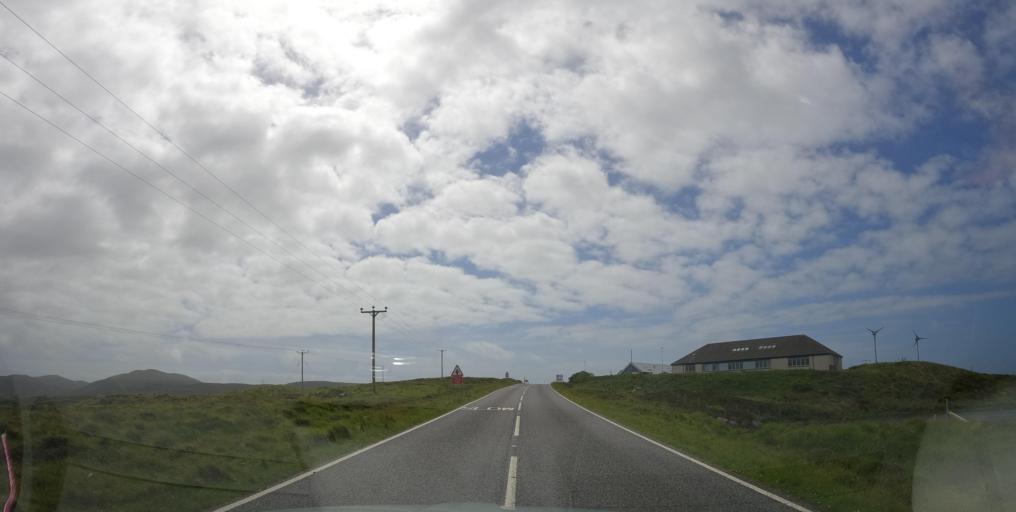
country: GB
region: Scotland
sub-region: Eilean Siar
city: Isle of South Uist
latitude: 57.2509
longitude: -7.3775
